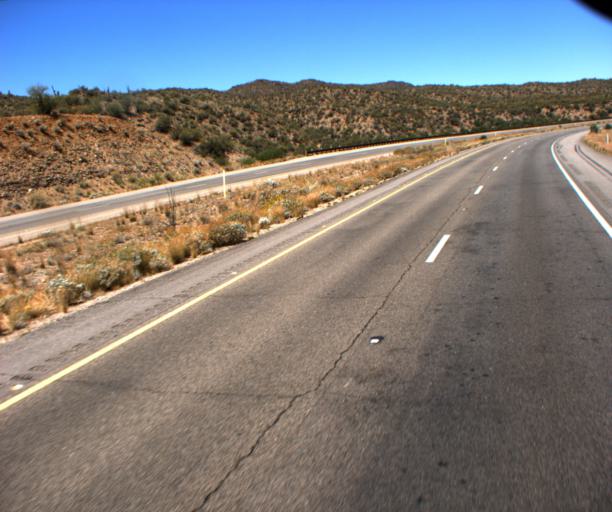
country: US
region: Arizona
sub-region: Yavapai County
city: Bagdad
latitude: 34.3884
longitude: -113.2056
